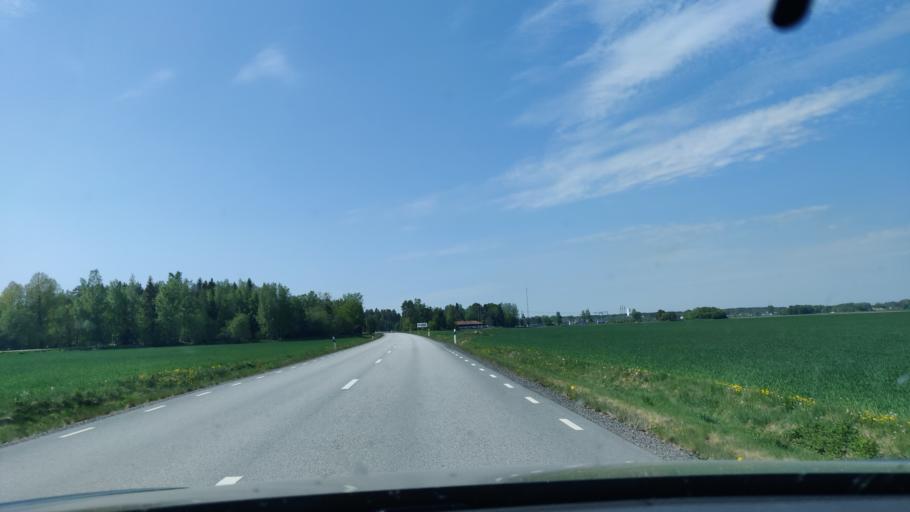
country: SE
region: Uppsala
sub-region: Heby Kommun
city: OEstervala
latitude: 60.1634
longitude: 17.1996
